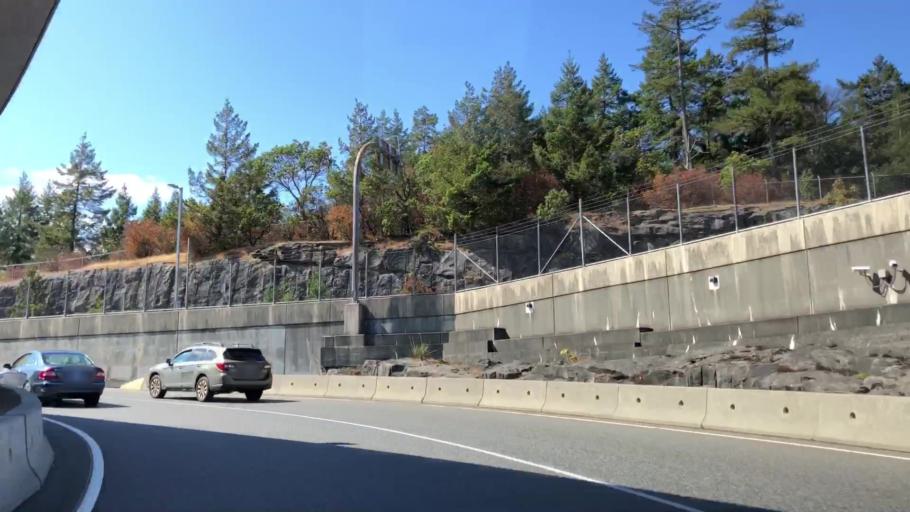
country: CA
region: British Columbia
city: Nanaimo
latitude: 49.1617
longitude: -123.8924
